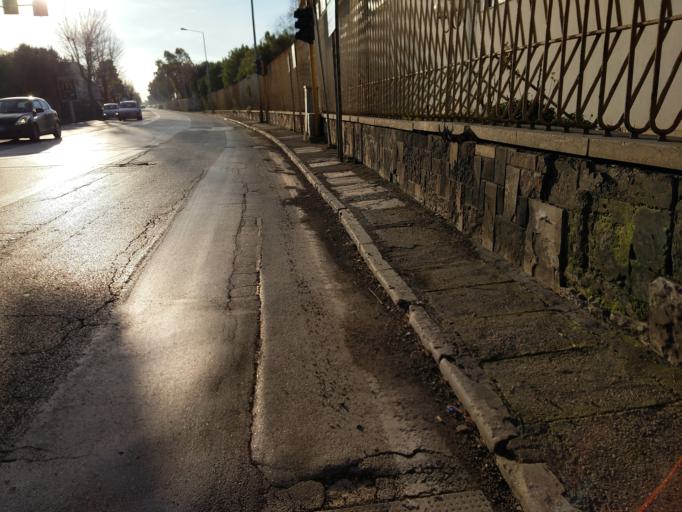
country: IT
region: Apulia
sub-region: Provincia di Bari
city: Bari
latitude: 41.1163
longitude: 16.8366
